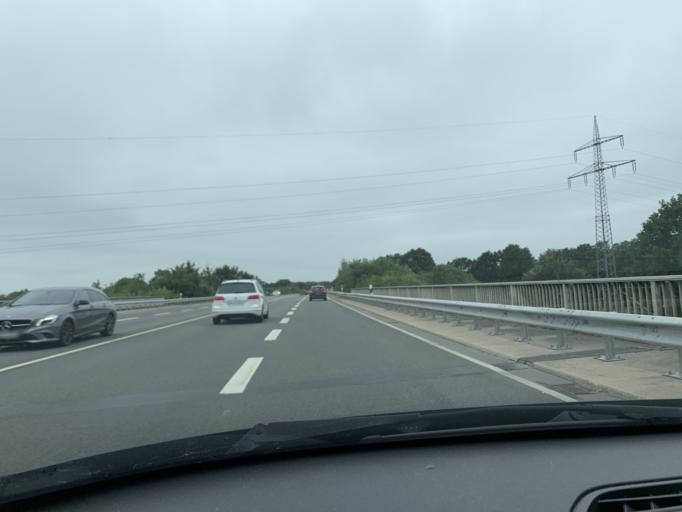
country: DE
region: Lower Saxony
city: Lingen
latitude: 52.4927
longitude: 7.3035
